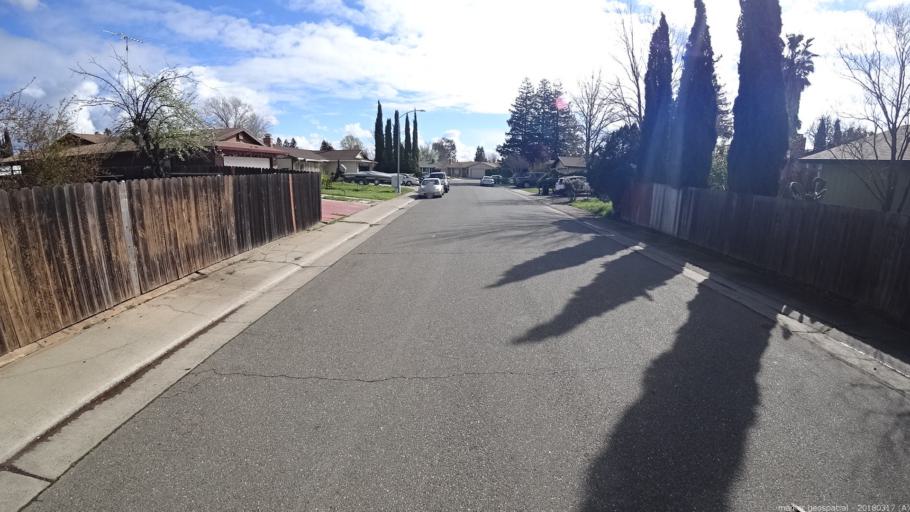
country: US
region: California
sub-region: Sacramento County
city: Florin
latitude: 38.4719
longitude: -121.3926
